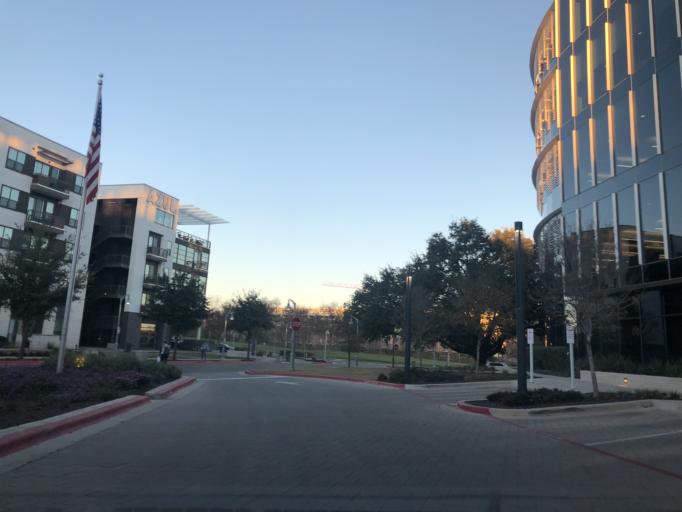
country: US
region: Texas
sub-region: Travis County
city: Austin
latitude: 30.2431
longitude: -97.7219
